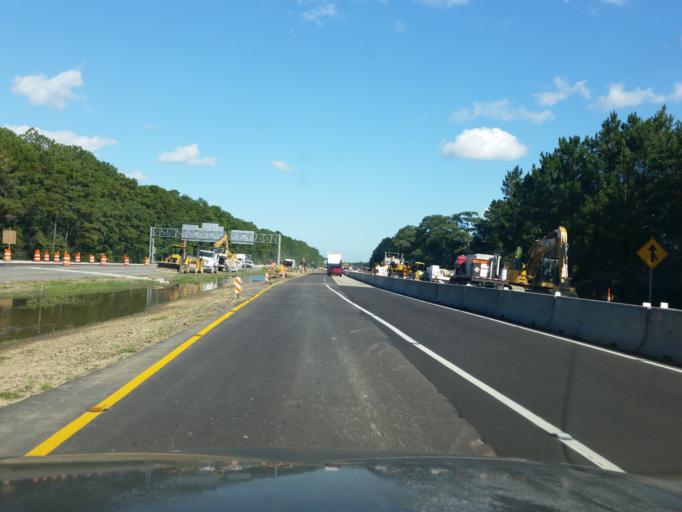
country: US
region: Louisiana
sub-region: Saint Tammany Parish
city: Slidell
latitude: 30.3038
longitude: -89.7334
